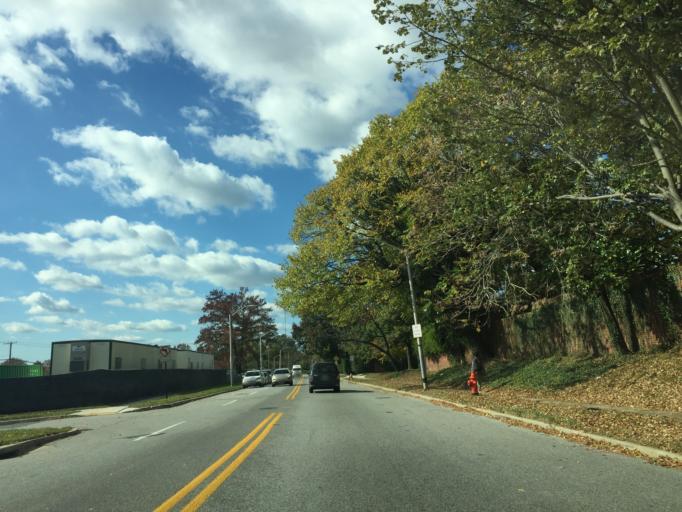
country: US
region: Maryland
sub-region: City of Baltimore
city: Baltimore
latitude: 39.3460
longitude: -76.6138
